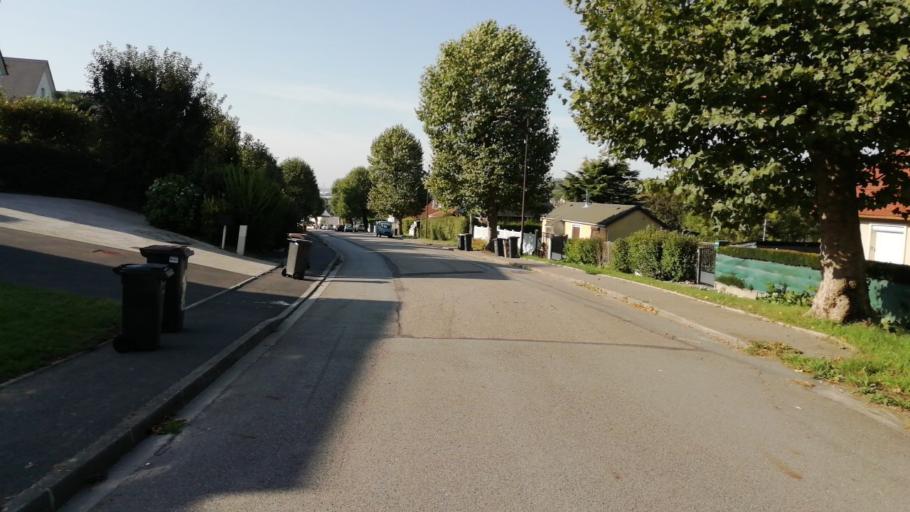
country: FR
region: Haute-Normandie
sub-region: Departement de la Seine-Maritime
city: Harfleur
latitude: 49.5149
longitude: 0.2024
